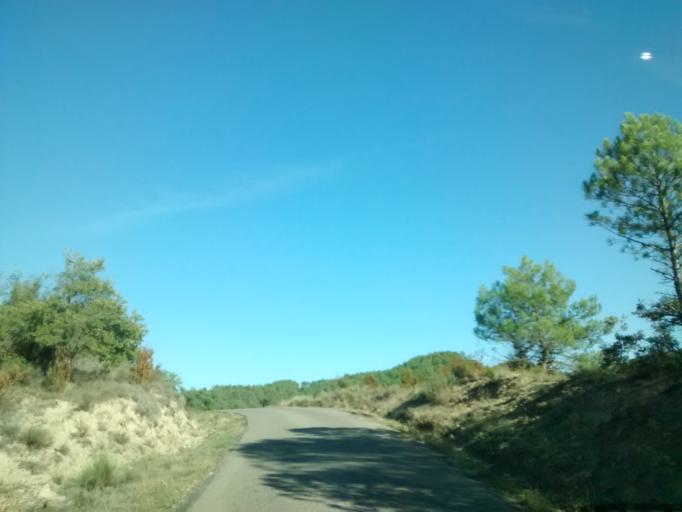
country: ES
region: Aragon
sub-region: Provincia de Huesca
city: Santa Cruz de la Seros
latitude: 42.4330
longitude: -0.6489
